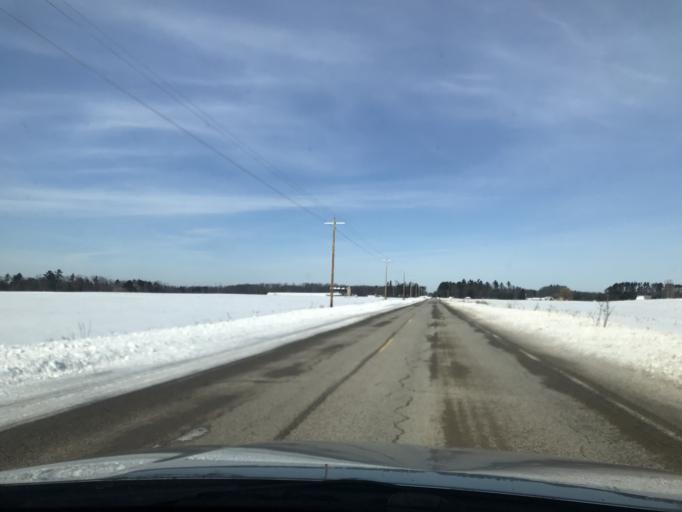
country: US
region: Wisconsin
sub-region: Oconto County
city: Oconto Falls
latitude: 45.1274
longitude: -88.1779
